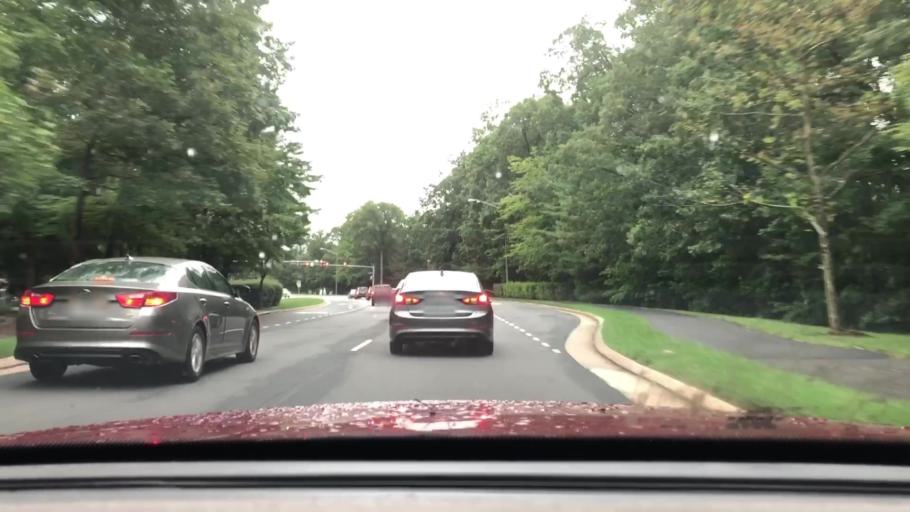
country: US
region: Virginia
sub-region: Fairfax County
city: Greenbriar
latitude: 38.8595
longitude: -77.3974
